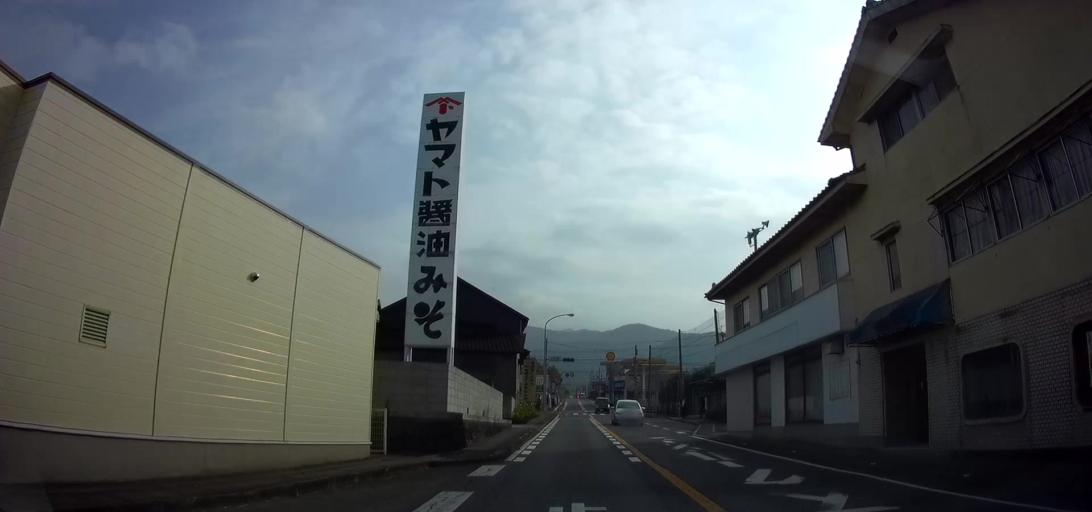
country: JP
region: Nagasaki
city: Shimabara
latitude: 32.7852
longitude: 130.2003
